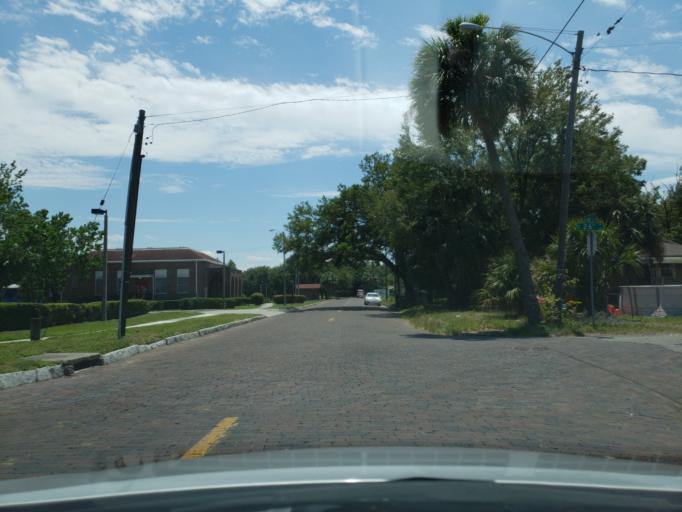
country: US
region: Florida
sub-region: Hillsborough County
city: Tampa
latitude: 27.9747
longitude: -82.4561
